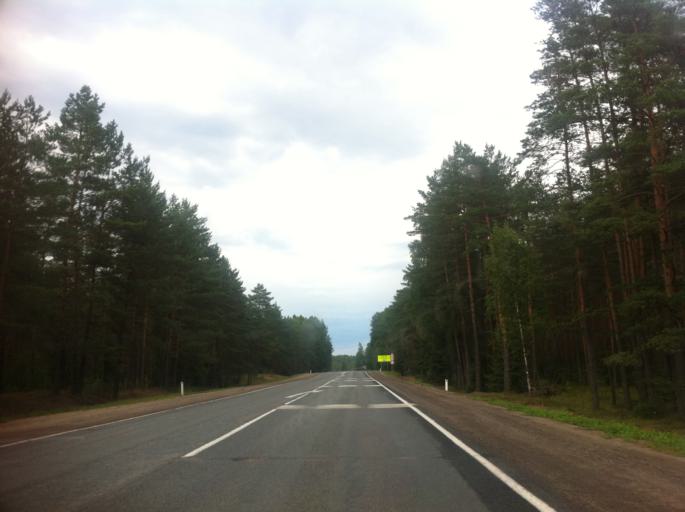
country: RU
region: Pskov
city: Pskov
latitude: 57.9447
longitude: 28.7233
